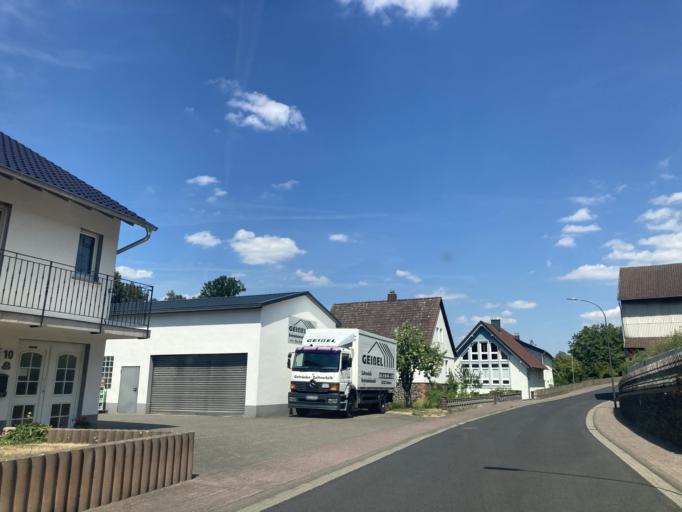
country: DE
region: Hesse
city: Grebenau
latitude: 50.7214
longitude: 9.4234
